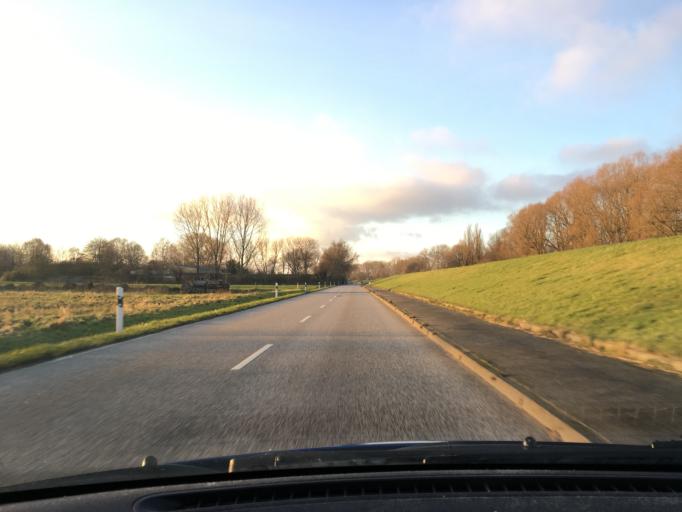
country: DE
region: Hamburg
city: Harburg
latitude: 53.4682
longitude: 10.0411
